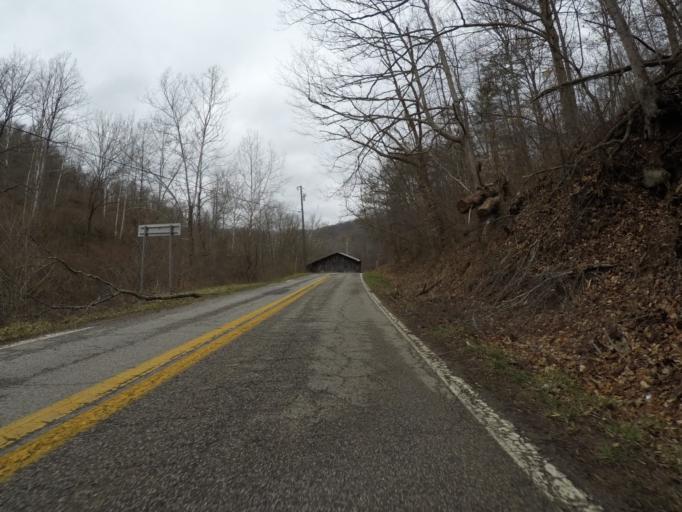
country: US
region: West Virginia
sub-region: Cabell County
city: Lesage
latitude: 38.4665
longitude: -82.2790
